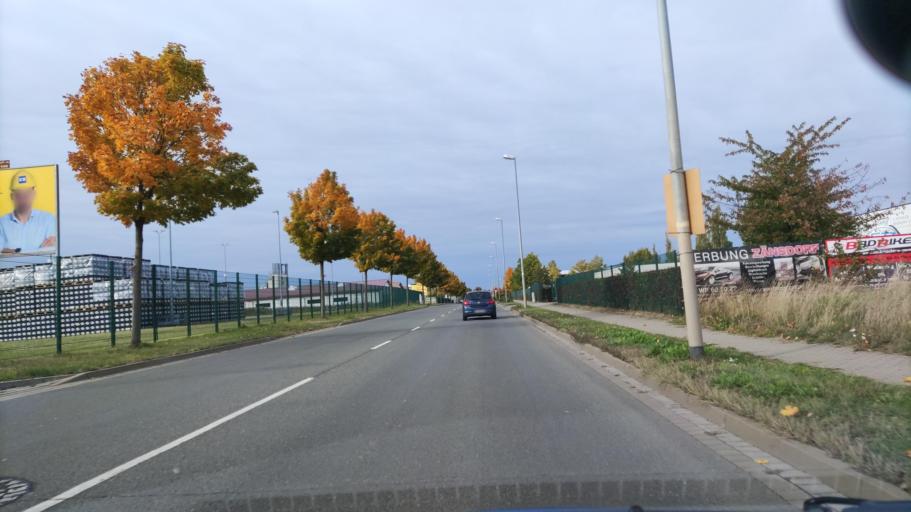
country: DE
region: Saxony-Anhalt
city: Wernigerode
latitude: 51.8456
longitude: 10.7574
